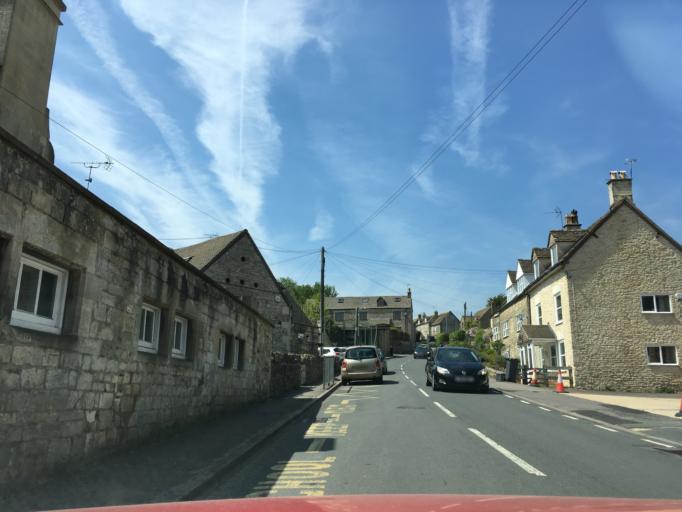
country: GB
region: England
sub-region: Gloucestershire
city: Nailsworth
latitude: 51.6812
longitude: -2.2353
